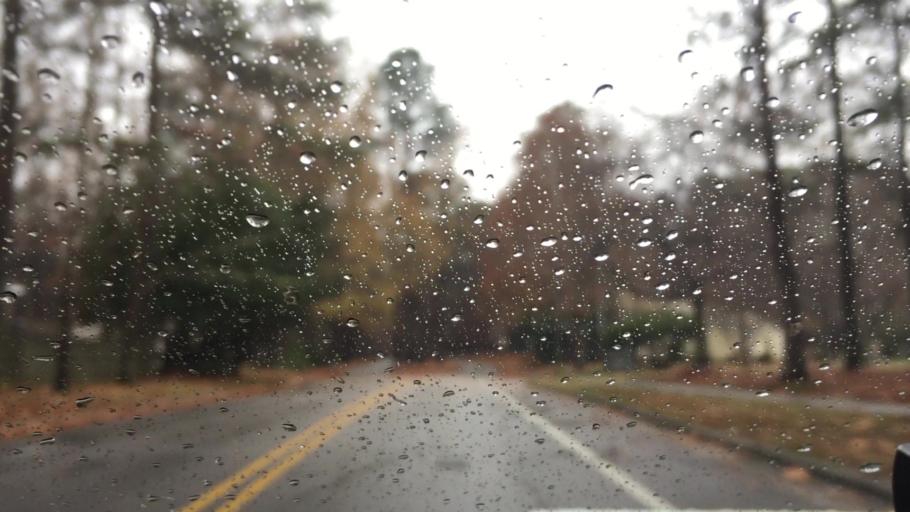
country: US
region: North Carolina
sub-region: Wake County
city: Cary
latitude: 35.7604
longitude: -78.7924
